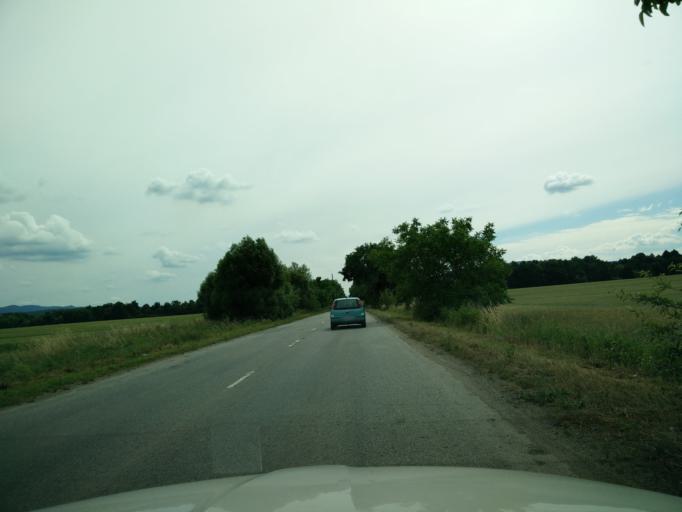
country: SK
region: Nitriansky
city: Novaky
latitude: 48.7368
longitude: 18.5705
